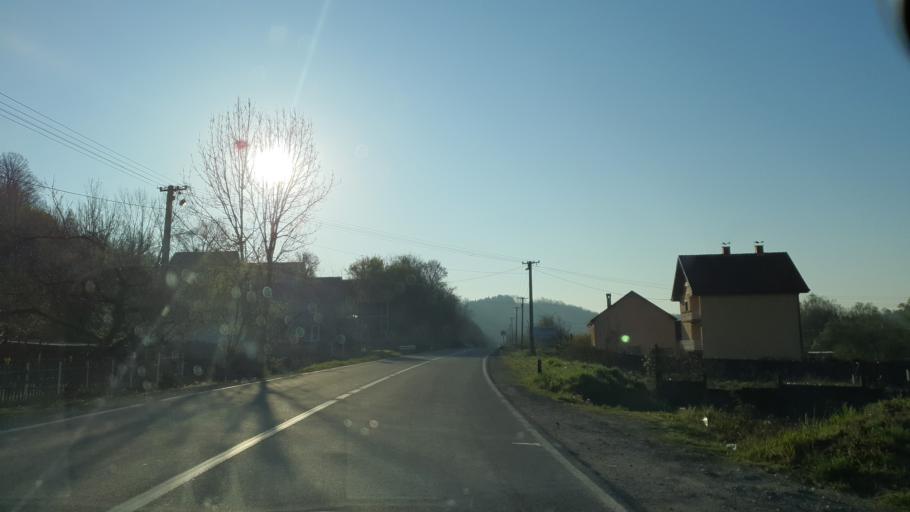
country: RS
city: Bukor
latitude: 44.4511
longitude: 19.4882
